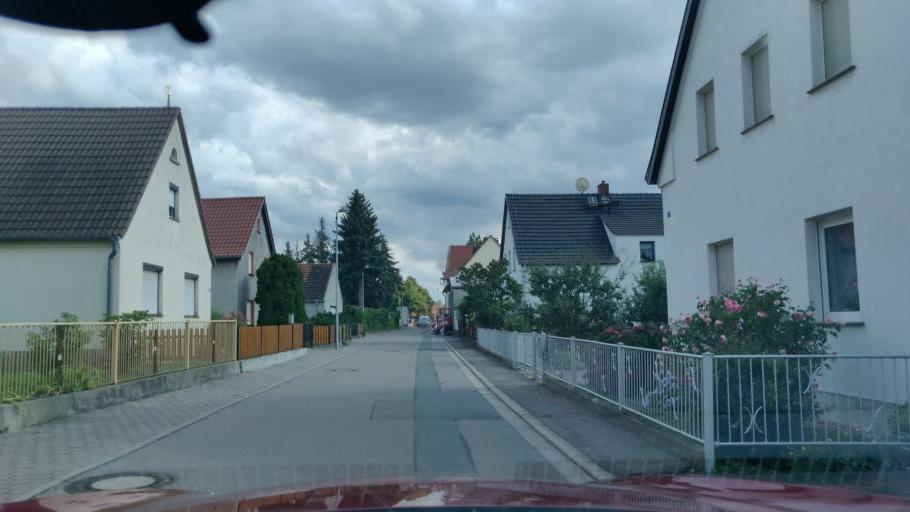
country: DE
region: Saxony
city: Schildau
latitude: 51.4917
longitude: 12.9016
